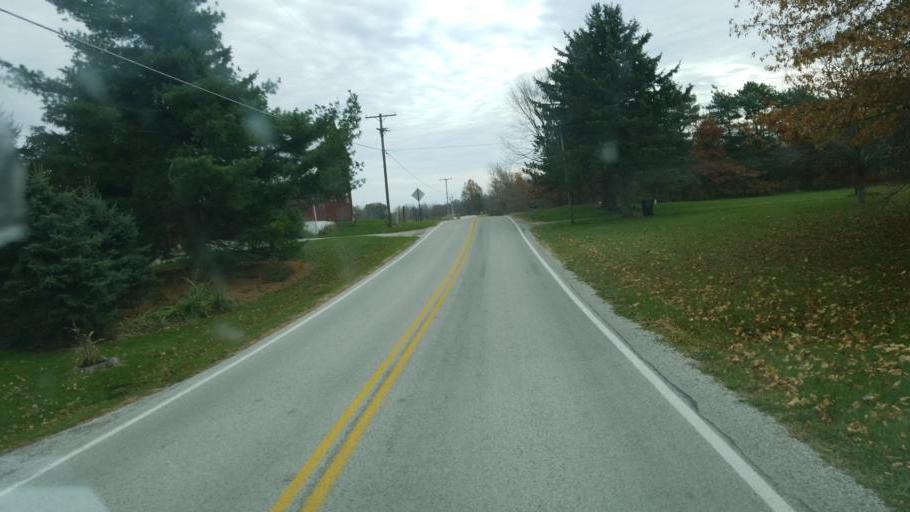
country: US
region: Ohio
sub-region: Crawford County
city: Crestline
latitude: 40.7314
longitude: -82.6866
